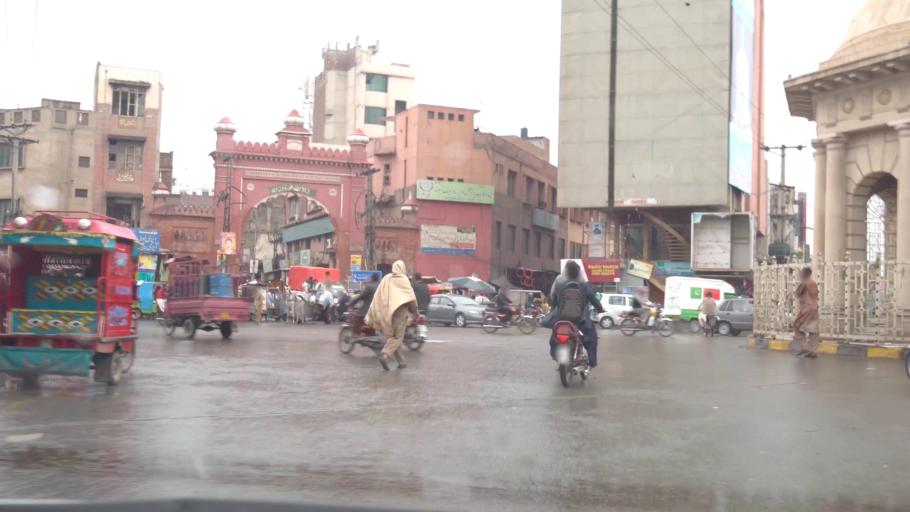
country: PK
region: Punjab
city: Faisalabad
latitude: 31.4166
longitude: 73.0888
